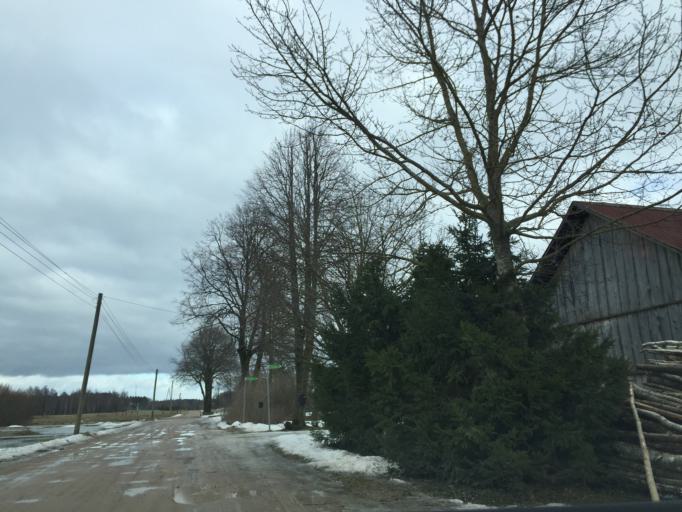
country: LV
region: Salacgrivas
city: Ainazi
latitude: 57.8493
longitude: 24.4849
